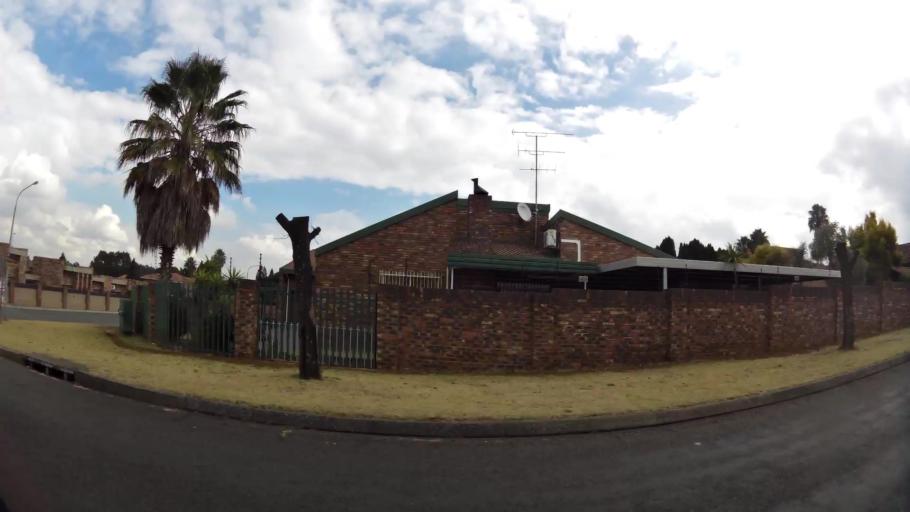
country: ZA
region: Gauteng
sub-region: Sedibeng District Municipality
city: Vanderbijlpark
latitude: -26.7405
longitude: 27.8547
